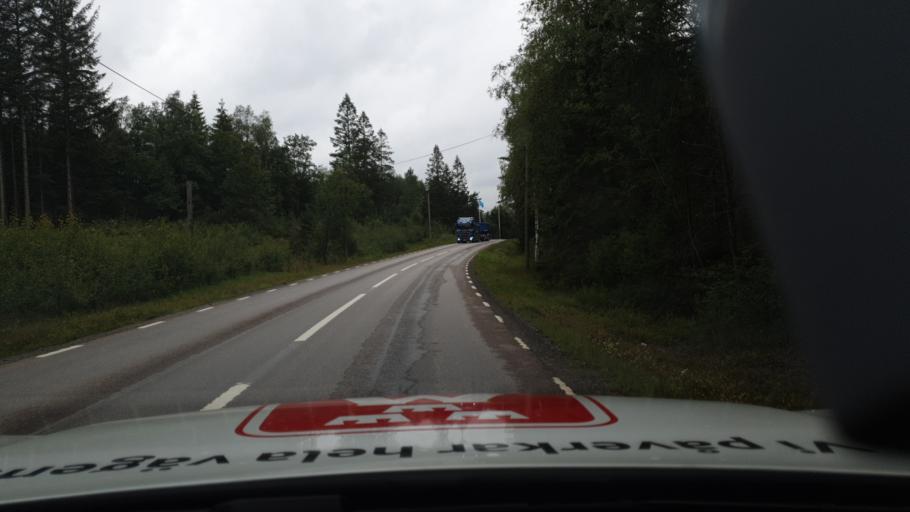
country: SE
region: Vaestra Goetaland
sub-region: Uddevalla Kommun
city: Ljungskile
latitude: 58.1760
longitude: 11.9979
